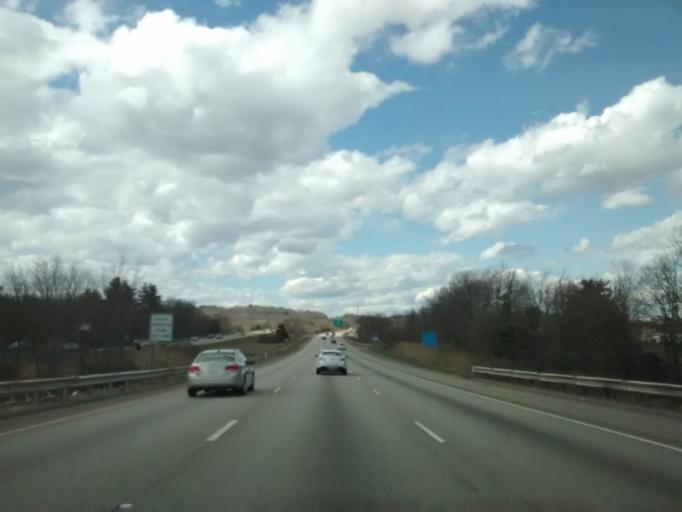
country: US
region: Massachusetts
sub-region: Worcester County
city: Cordaville
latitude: 42.2705
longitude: -71.5648
